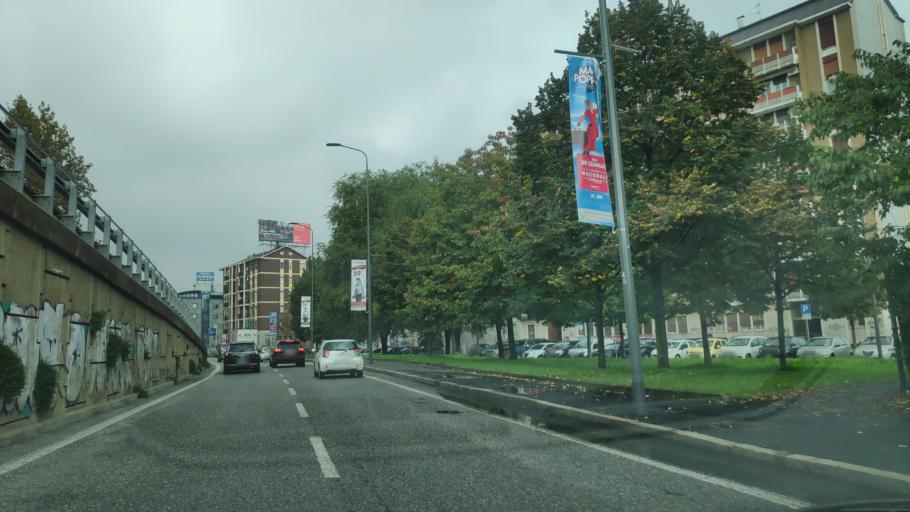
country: IT
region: Lombardy
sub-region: Citta metropolitana di Milano
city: Milano
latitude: 45.4388
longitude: 9.1720
